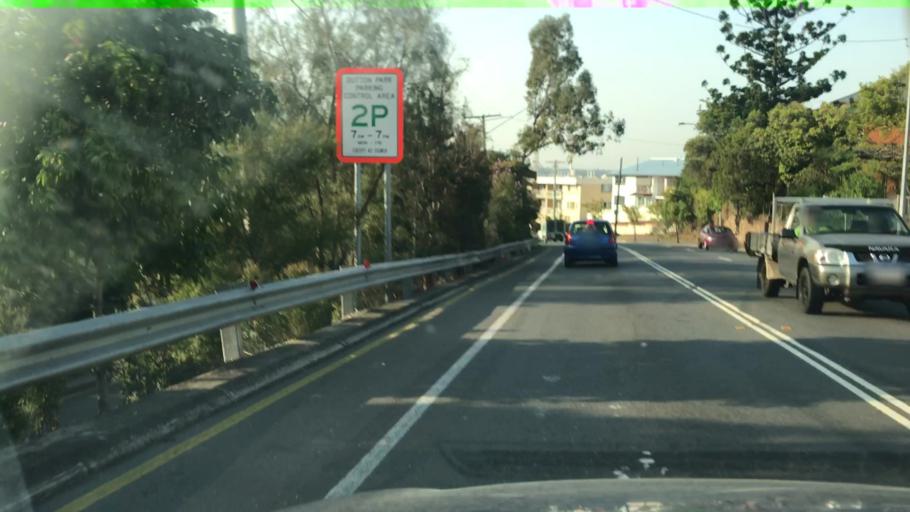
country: AU
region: Queensland
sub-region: Brisbane
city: South Brisbane
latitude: -27.4896
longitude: 153.0186
